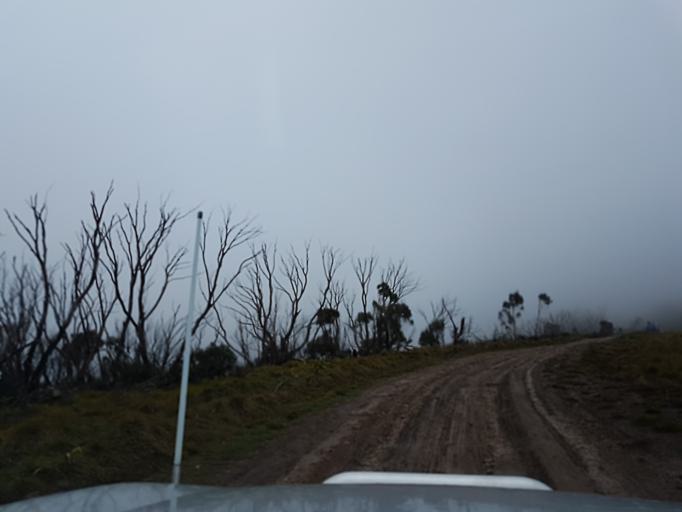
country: AU
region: Victoria
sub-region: Alpine
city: Mount Beauty
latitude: -37.0858
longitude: 147.1088
